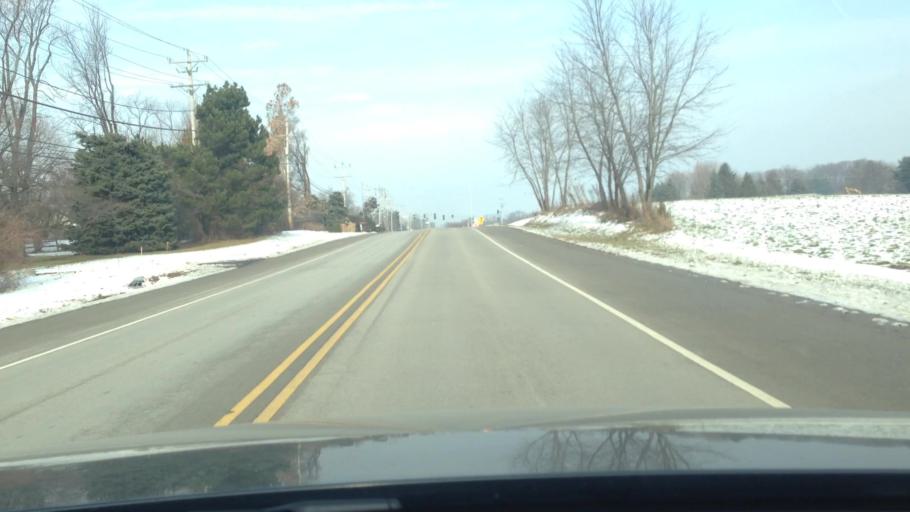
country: US
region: Illinois
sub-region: Will County
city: Lockport
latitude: 41.5949
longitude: -88.0072
